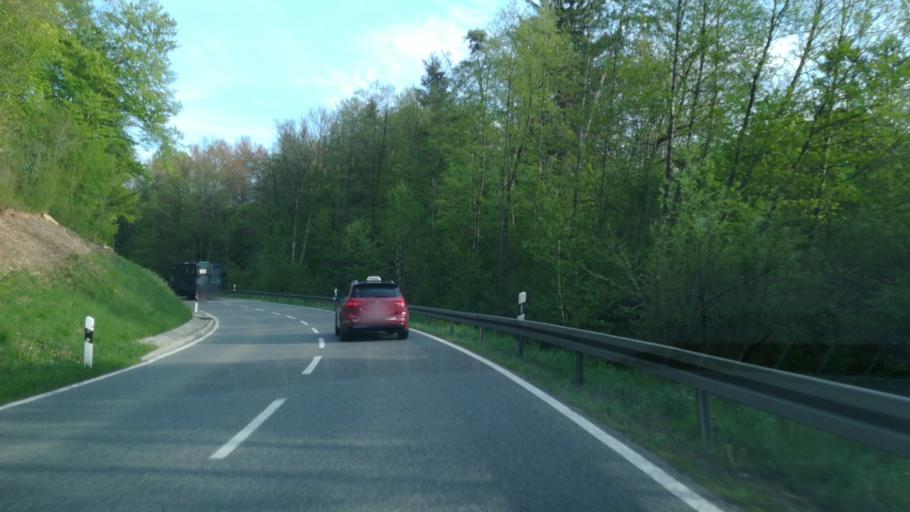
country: DE
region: Baden-Wuerttemberg
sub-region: Freiburg Region
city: Muhlingen
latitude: 47.8978
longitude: 9.0068
